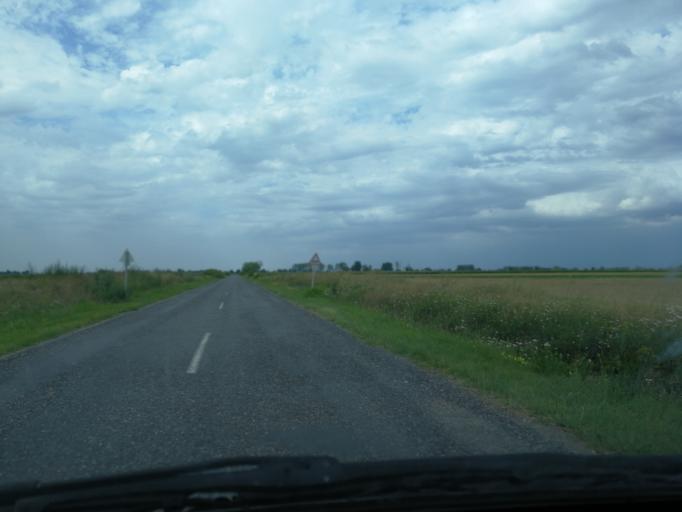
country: HU
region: Bacs-Kiskun
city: Kalocsa
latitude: 46.4833
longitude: 19.0509
